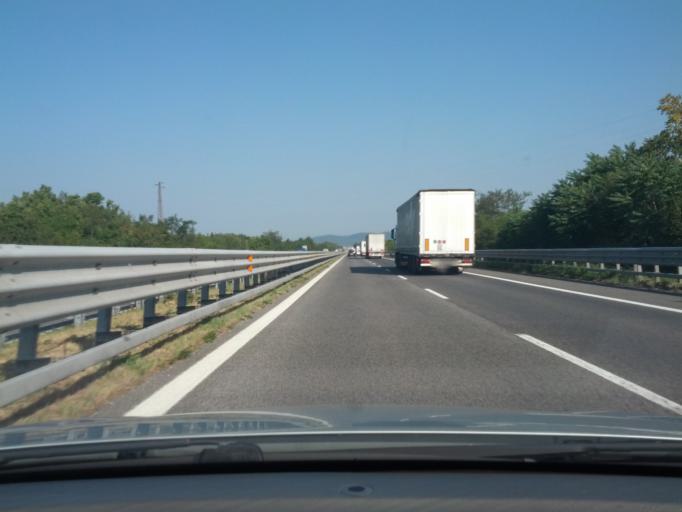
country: IT
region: Friuli Venezia Giulia
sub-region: Provincia di Trieste
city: Prosecco-Contovello
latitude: 45.7256
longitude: 13.7182
